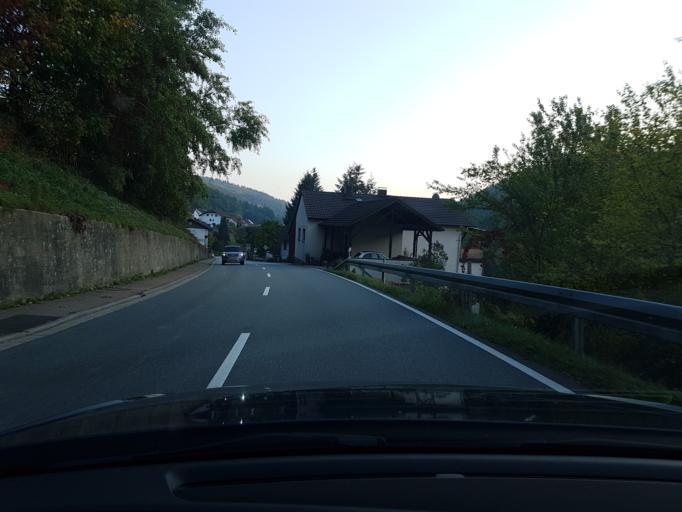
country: DE
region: Hesse
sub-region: Regierungsbezirk Darmstadt
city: Beerfelden
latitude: 49.5208
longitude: 8.9657
